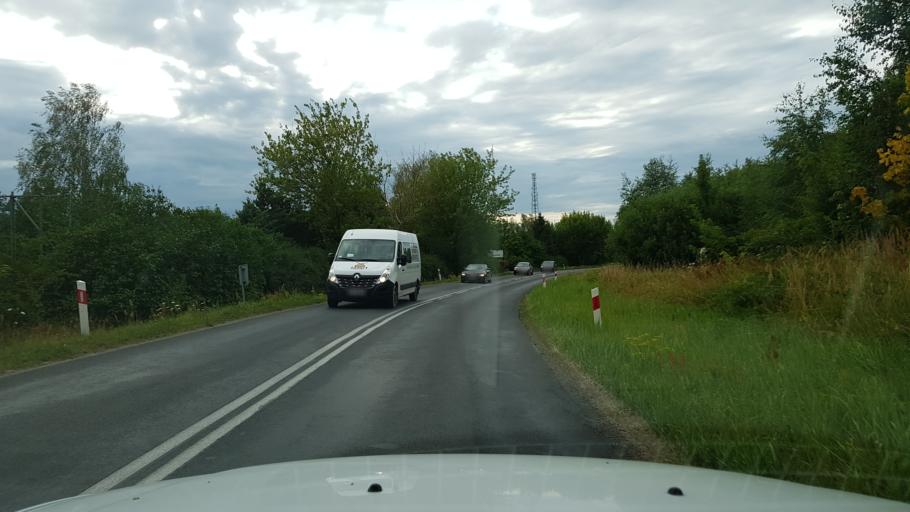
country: PL
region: West Pomeranian Voivodeship
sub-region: Powiat kolobrzeski
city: Kolobrzeg
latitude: 54.1459
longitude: 15.6465
